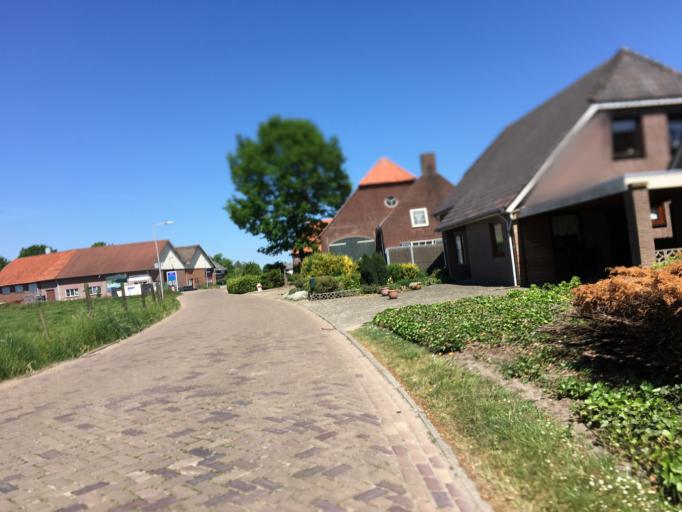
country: NL
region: North Brabant
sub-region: Gemeente Heusden
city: Heusden
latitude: 51.7327
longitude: 5.1578
